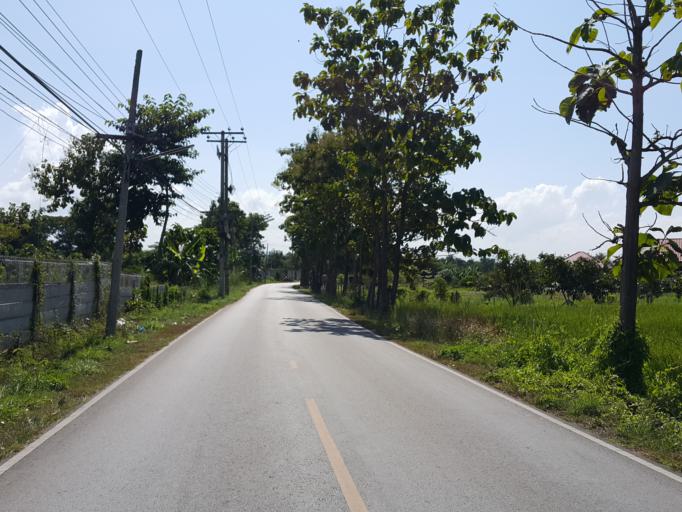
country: TH
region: Chiang Mai
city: San Sai
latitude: 18.8531
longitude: 99.1430
